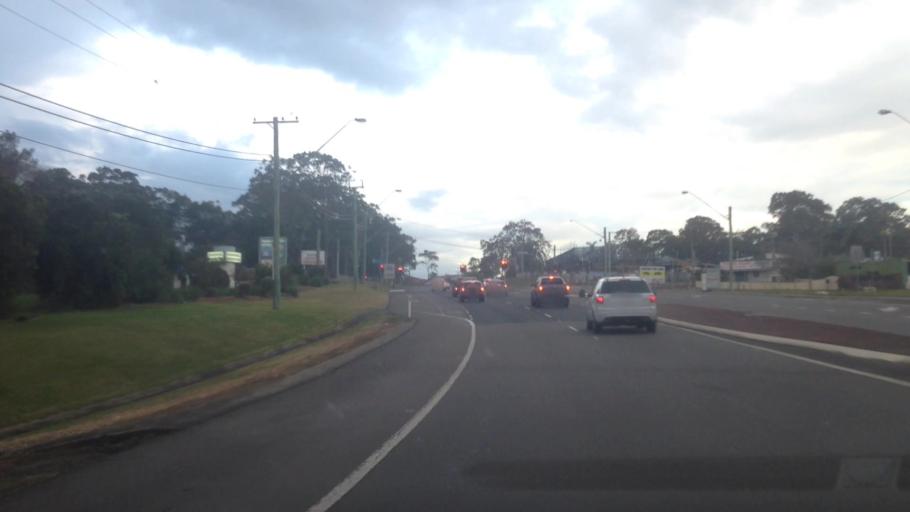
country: AU
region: New South Wales
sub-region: Wyong Shire
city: Kanwal
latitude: -33.2631
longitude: 151.4801
